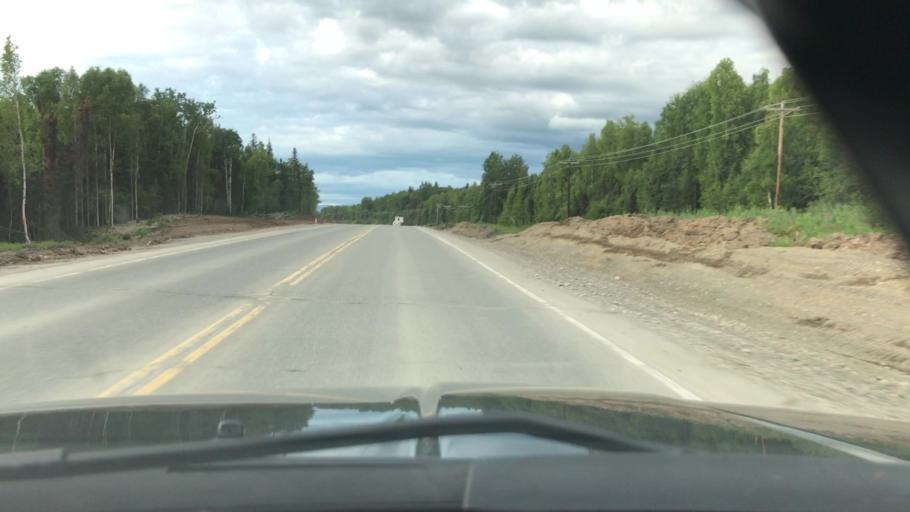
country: US
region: Alaska
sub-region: Matanuska-Susitna Borough
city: Y
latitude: 62.1104
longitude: -150.0562
